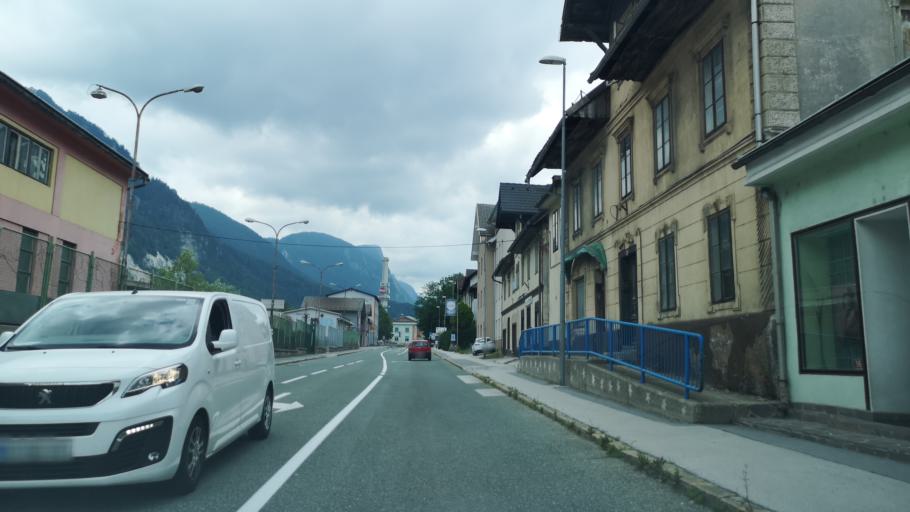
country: SI
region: Jesenice
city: Jesenice
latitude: 46.4313
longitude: 14.0672
